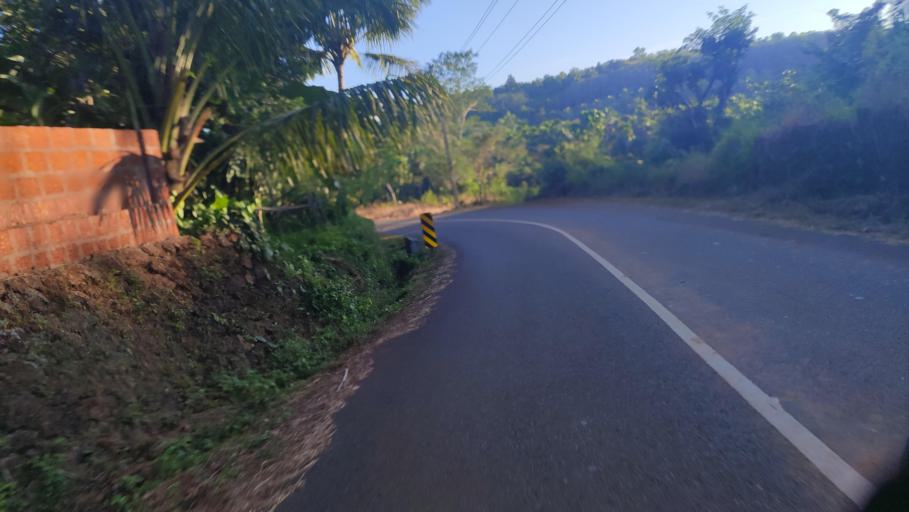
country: IN
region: Kerala
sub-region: Kasaragod District
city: Kasaragod
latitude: 12.4535
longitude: 75.0977
